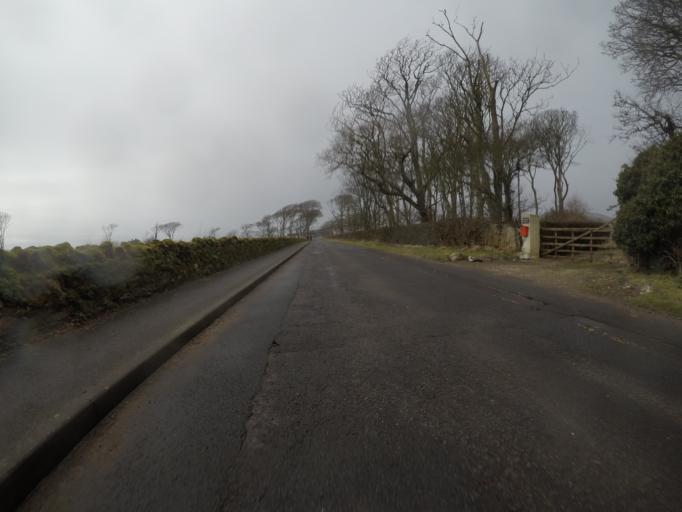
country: GB
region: Scotland
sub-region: North Ayrshire
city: West Kilbride
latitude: 55.6961
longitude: -4.8782
